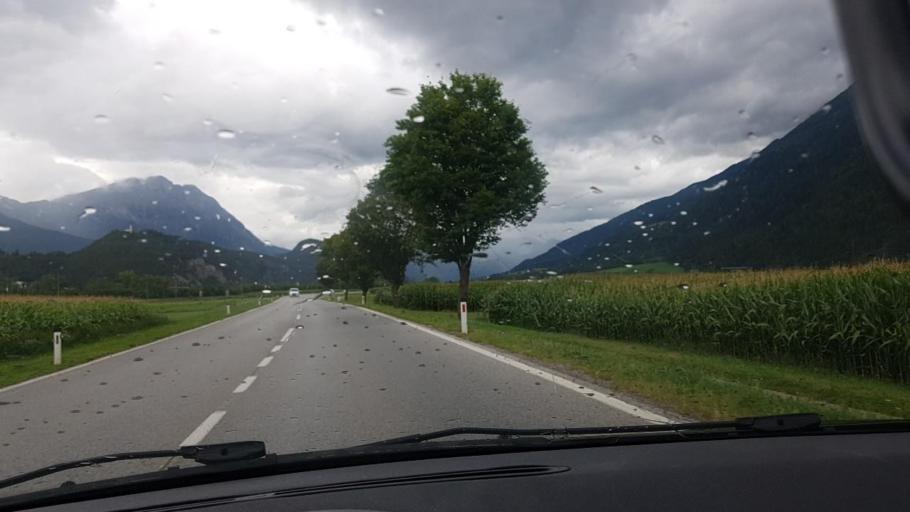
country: AT
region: Tyrol
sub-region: Politischer Bezirk Imst
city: Silz
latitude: 47.2695
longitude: 10.9425
